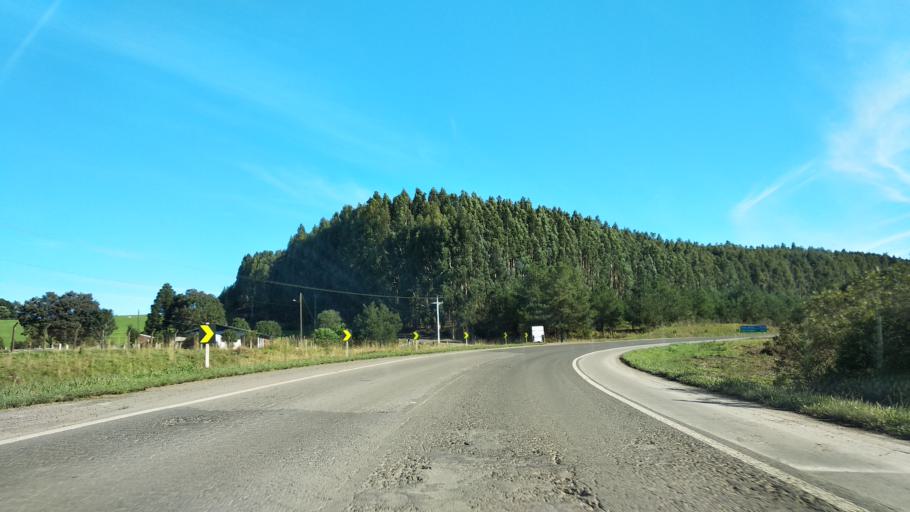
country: BR
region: Santa Catarina
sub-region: Campos Novos
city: Campos Novos
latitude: -27.3983
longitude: -51.1947
